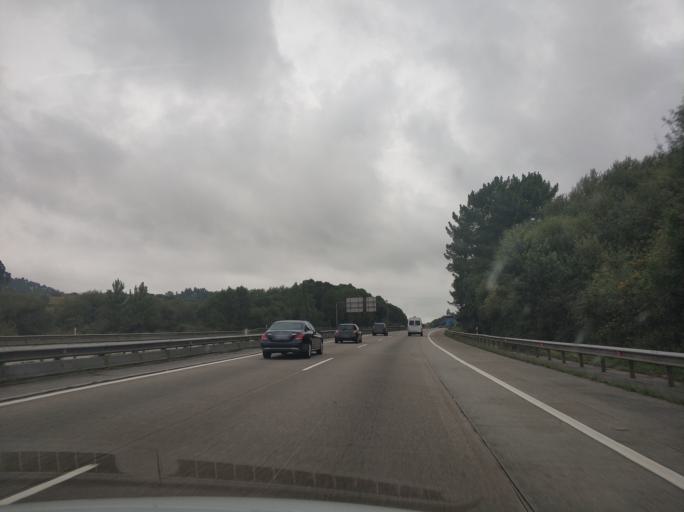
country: ES
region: Asturias
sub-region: Province of Asturias
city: Corvera de Asturias
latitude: 43.5052
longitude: -5.8045
